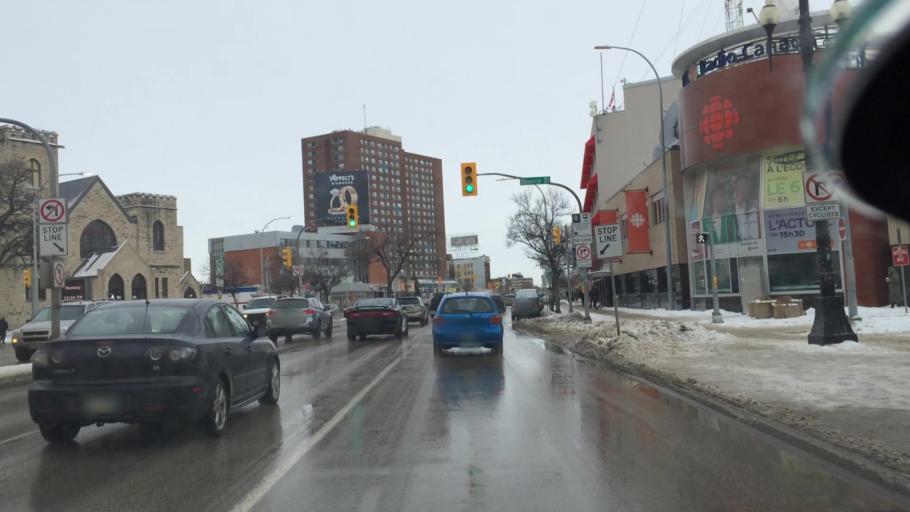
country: CA
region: Manitoba
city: Winnipeg
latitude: 49.8900
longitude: -97.1537
